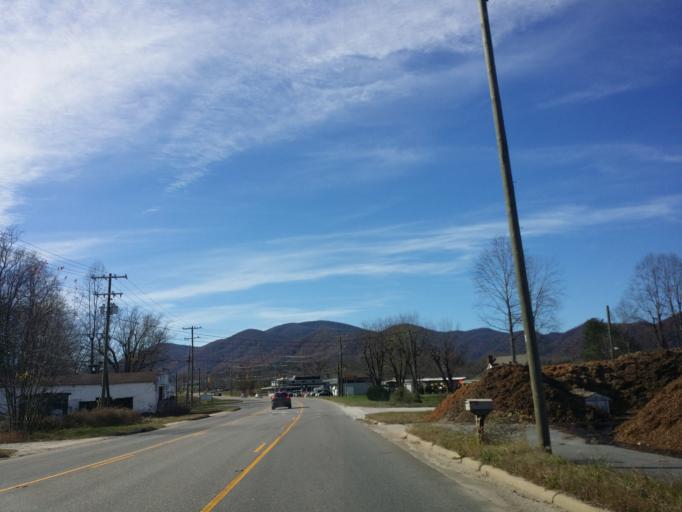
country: US
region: North Carolina
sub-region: McDowell County
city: West Marion
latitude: 35.6922
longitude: -82.0598
